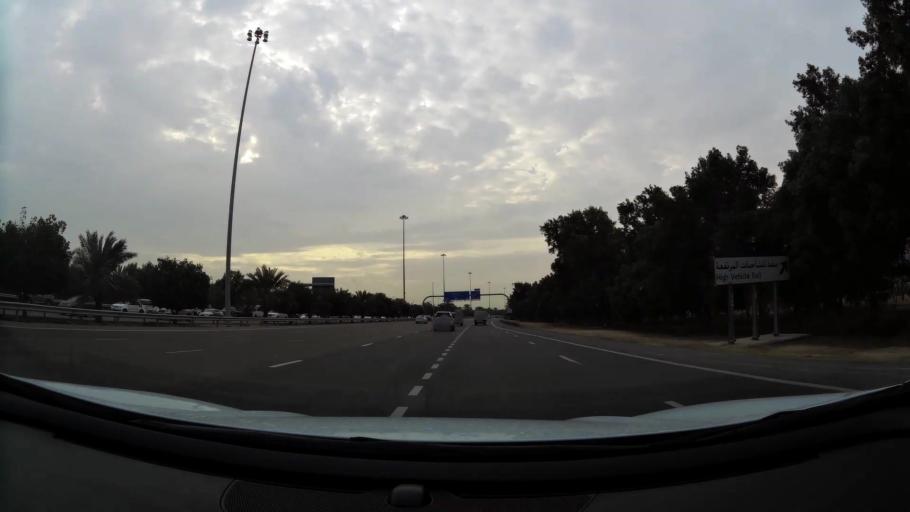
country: AE
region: Abu Dhabi
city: Abu Dhabi
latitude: 24.3634
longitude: 54.5626
